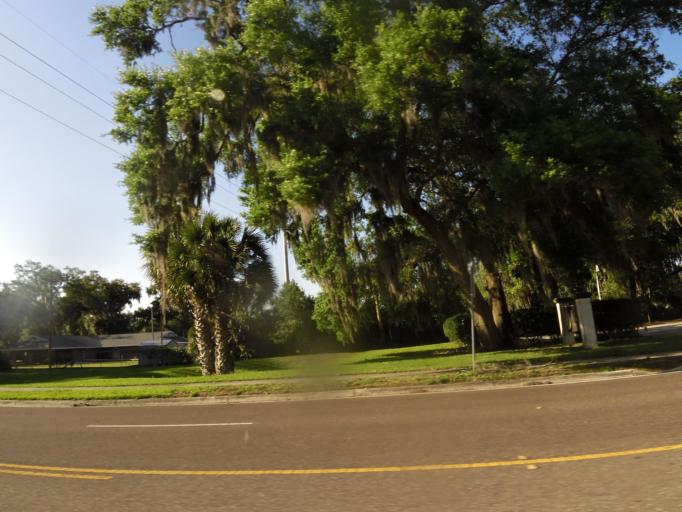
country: US
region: Florida
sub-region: Putnam County
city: Palatka
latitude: 29.6486
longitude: -81.6682
